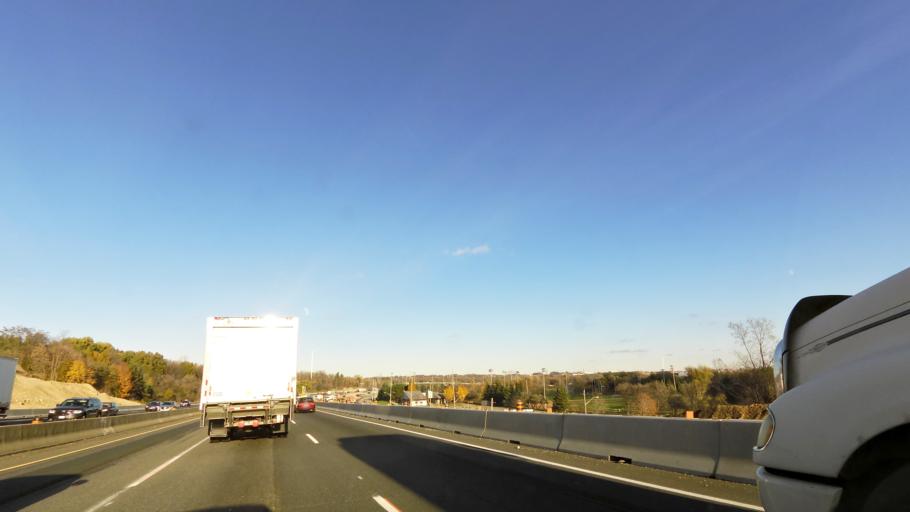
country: CA
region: Ontario
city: Cambridge
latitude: 43.4106
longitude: -80.3609
